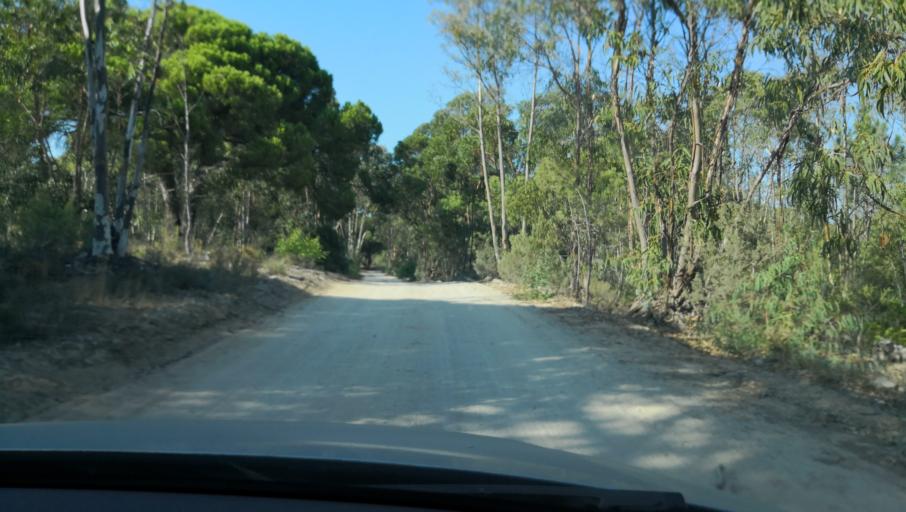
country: PT
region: Setubal
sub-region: Setubal
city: Setubal
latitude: 38.4751
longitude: -8.8791
